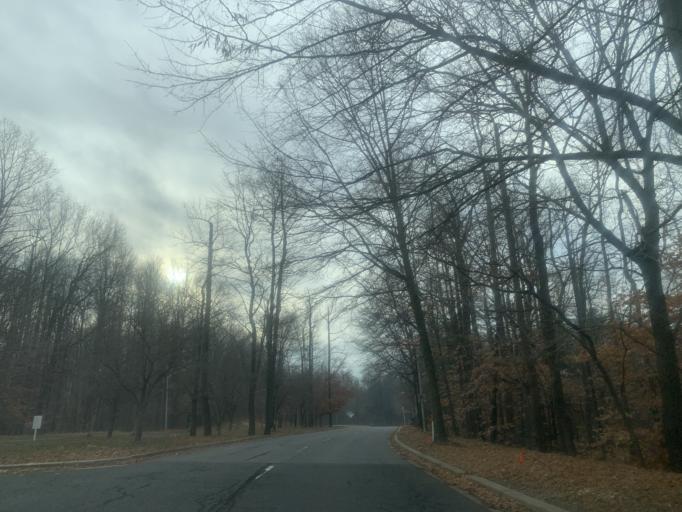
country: US
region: Maryland
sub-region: Prince George's County
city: Forestville
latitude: 38.8274
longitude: -76.8505
